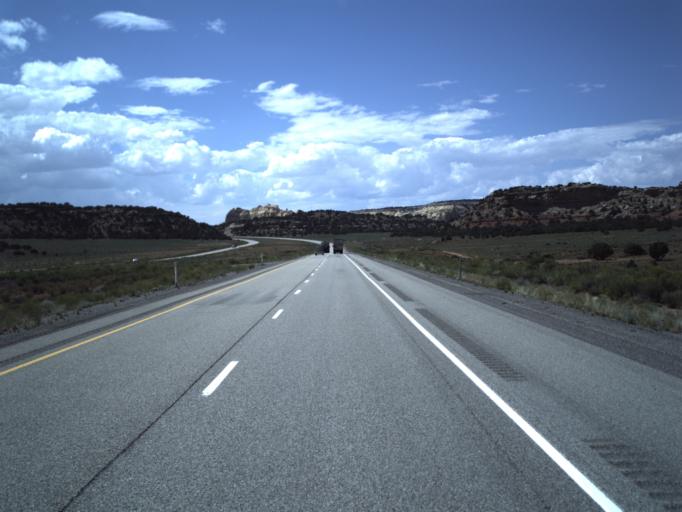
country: US
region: Utah
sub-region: Emery County
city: Castle Dale
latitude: 38.8720
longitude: -110.7298
